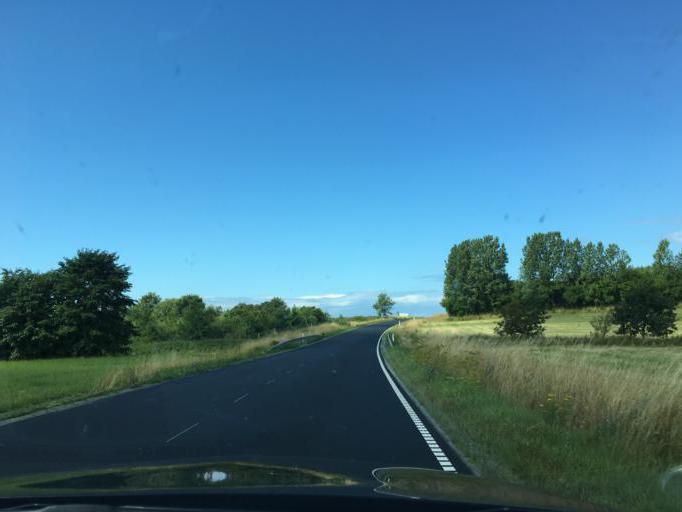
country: DK
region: Capital Region
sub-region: Gribskov Kommune
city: Helsinge
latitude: 56.0765
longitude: 12.1922
